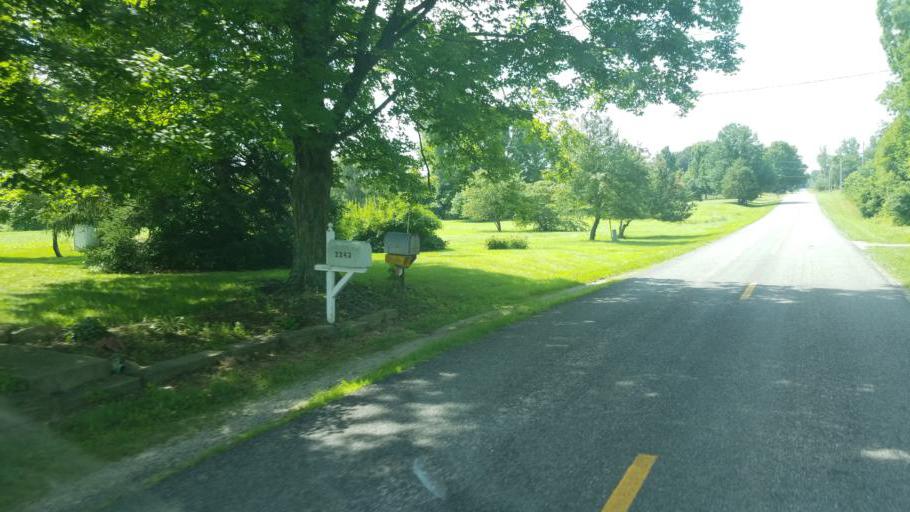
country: US
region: Ohio
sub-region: Delaware County
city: Sunbury
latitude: 40.3014
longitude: -82.9442
